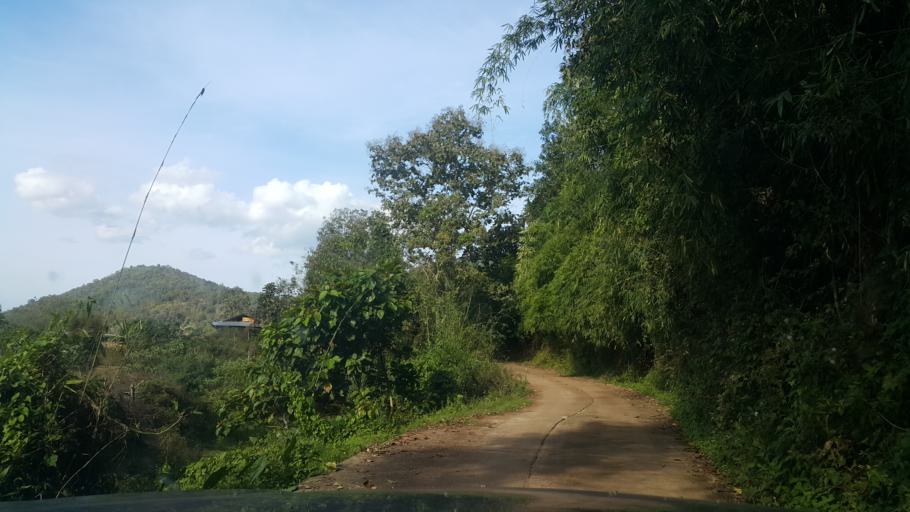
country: TH
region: Chiang Mai
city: Samoeng
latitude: 18.9653
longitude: 98.6791
